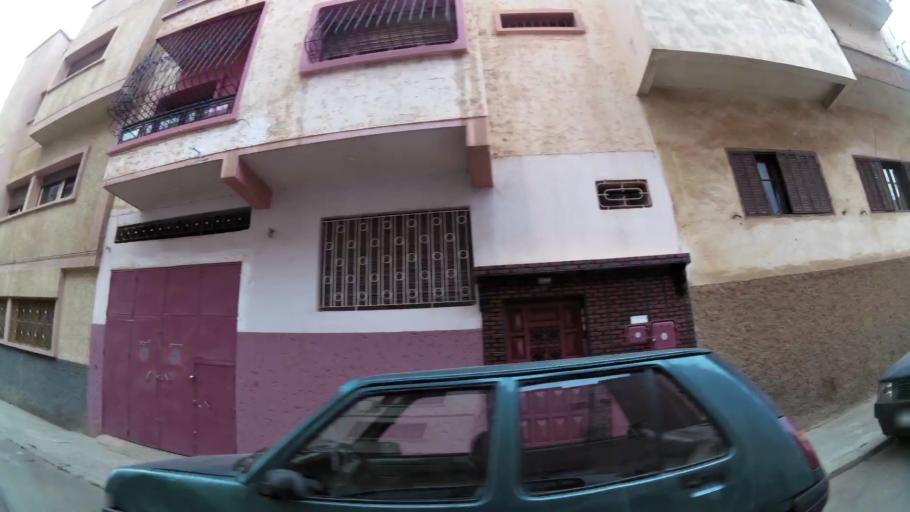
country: MA
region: Rabat-Sale-Zemmour-Zaer
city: Sale
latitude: 34.0433
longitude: -6.7963
